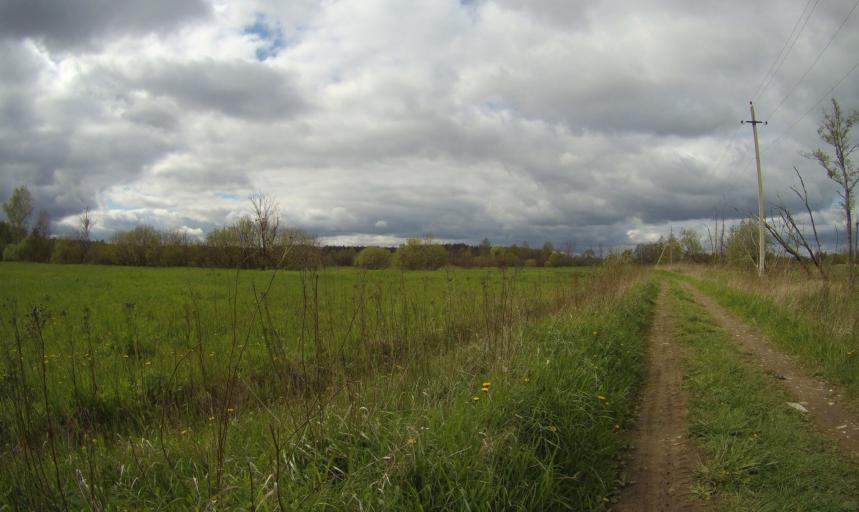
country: RU
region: Moskovskaya
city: Rechitsy
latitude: 55.5638
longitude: 38.4819
